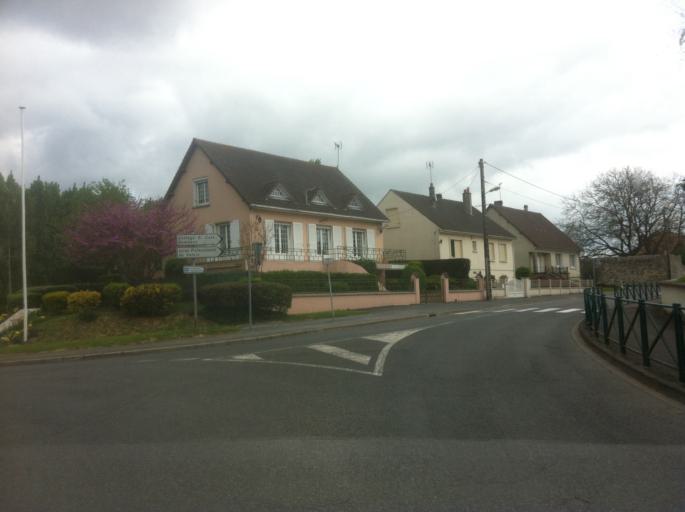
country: FR
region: Picardie
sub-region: Departement de l'Oise
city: Nanteuil-le-Haudouin
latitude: 49.1379
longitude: 2.8052
